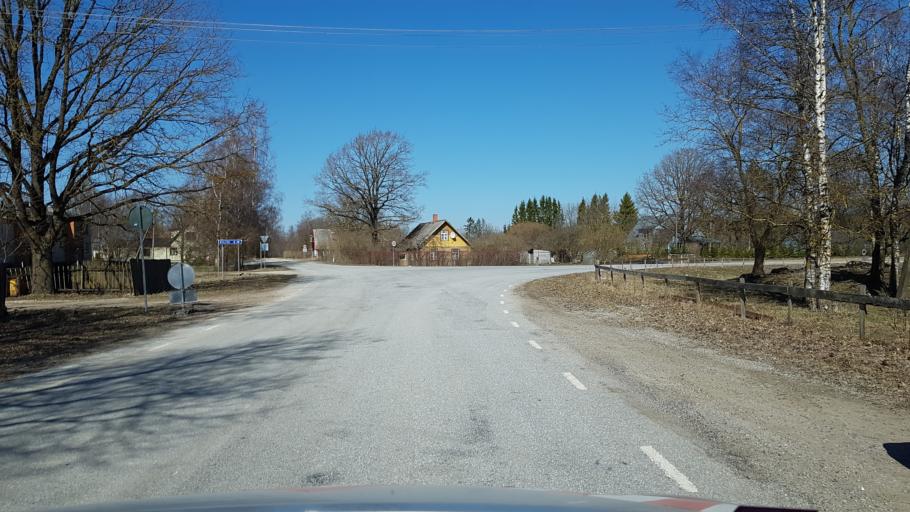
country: EE
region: Jaervamaa
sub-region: Koeru vald
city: Koeru
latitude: 59.0509
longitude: 26.0883
